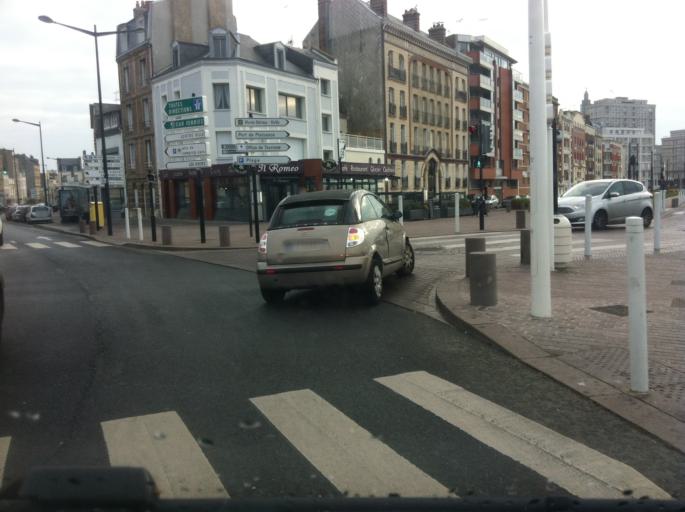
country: FR
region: Haute-Normandie
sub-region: Departement de la Seine-Maritime
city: Le Havre
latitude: 49.4957
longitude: 0.0939
